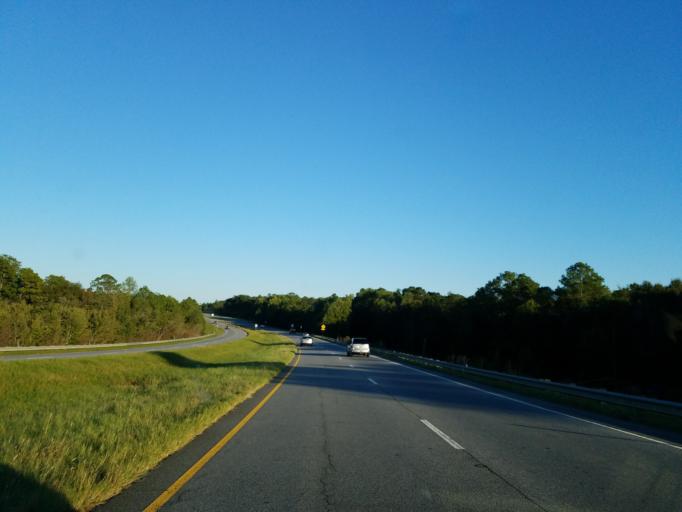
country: US
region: Georgia
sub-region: Worth County
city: Sylvester
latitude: 31.5116
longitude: -83.7753
